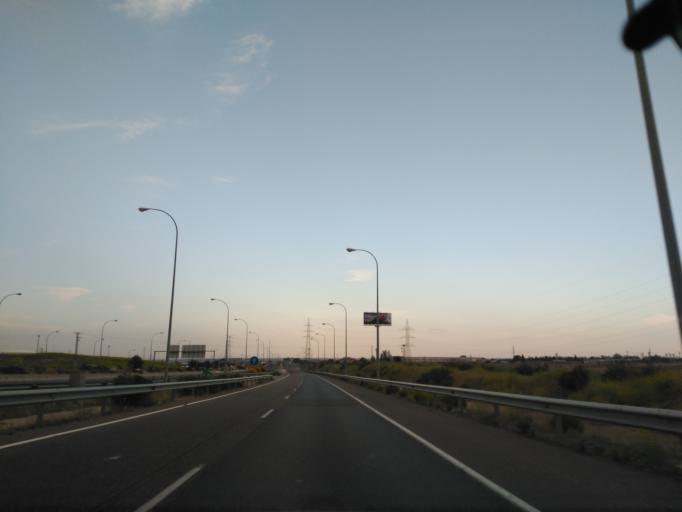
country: ES
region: Madrid
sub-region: Provincia de Madrid
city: Villaverde
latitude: 40.3253
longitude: -3.7037
